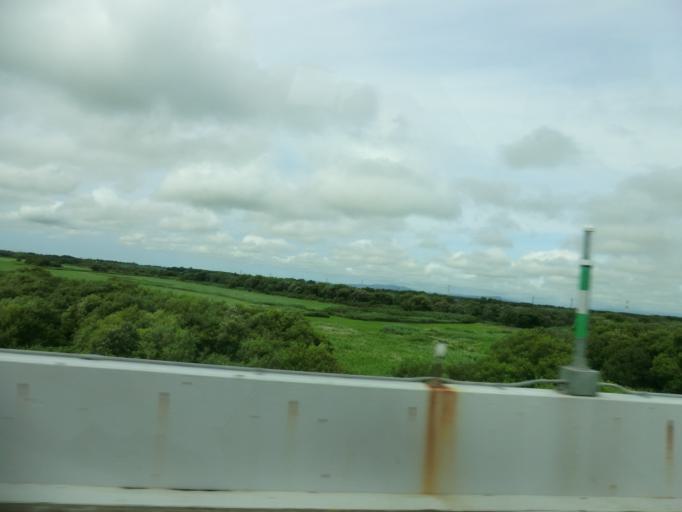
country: JP
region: Hokkaido
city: Ebetsu
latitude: 43.1140
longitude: 141.6169
